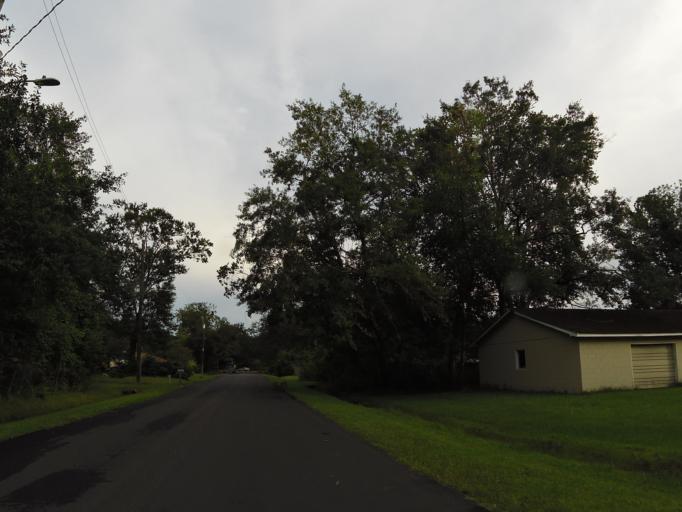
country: US
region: Florida
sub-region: Nassau County
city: Nassau Village-Ratliff
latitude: 30.4174
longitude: -81.7599
